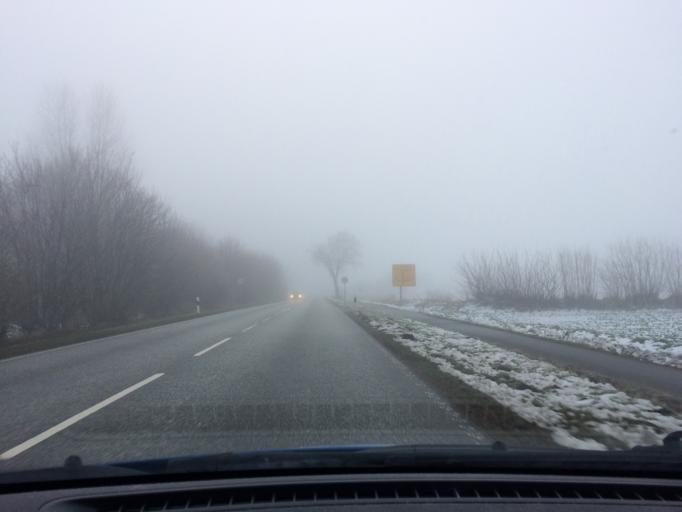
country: DE
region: Schleswig-Holstein
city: Grabau
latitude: 53.5226
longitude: 10.5061
